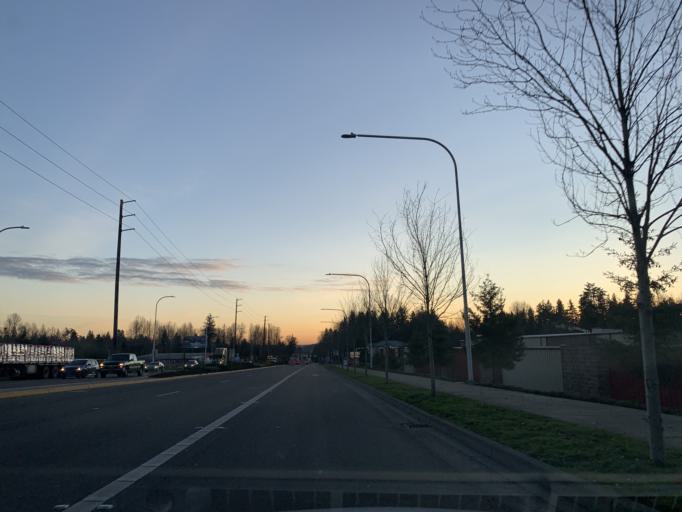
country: US
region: Washington
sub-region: Pierce County
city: Fife Heights
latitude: 47.2859
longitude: -122.3203
